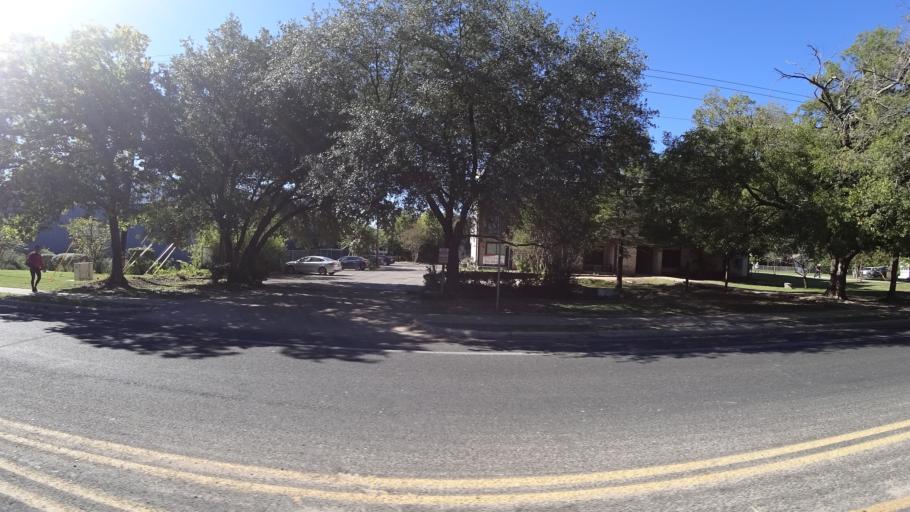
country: US
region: Texas
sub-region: Travis County
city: Austin
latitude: 30.2276
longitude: -97.7557
